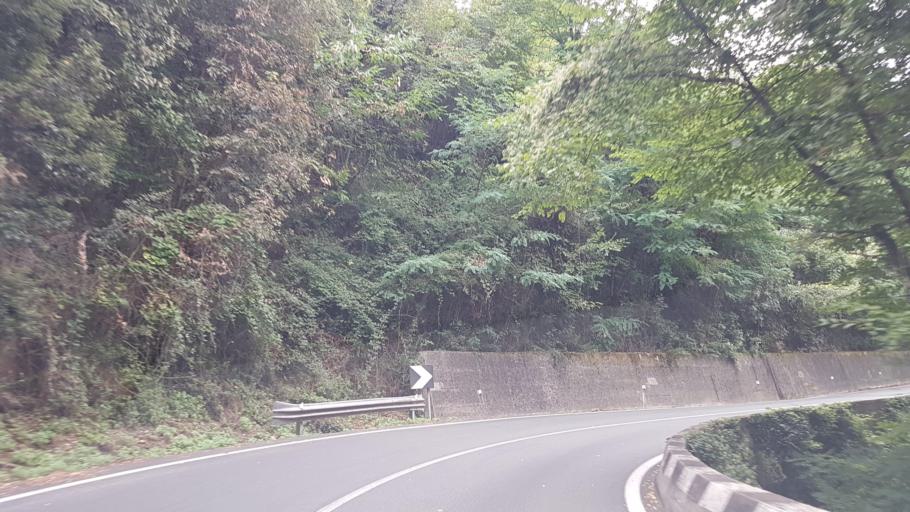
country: IT
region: Liguria
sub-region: Provincia di Genova
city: Casarza Ligure
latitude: 44.2567
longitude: 9.4696
